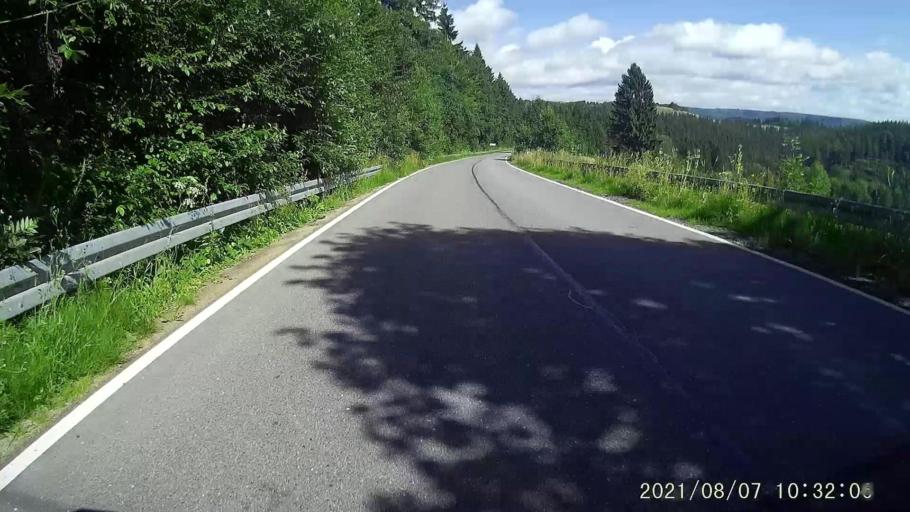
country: PL
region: Lower Silesian Voivodeship
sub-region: Powiat klodzki
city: Duszniki-Zdroj
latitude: 50.3916
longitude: 16.3552
